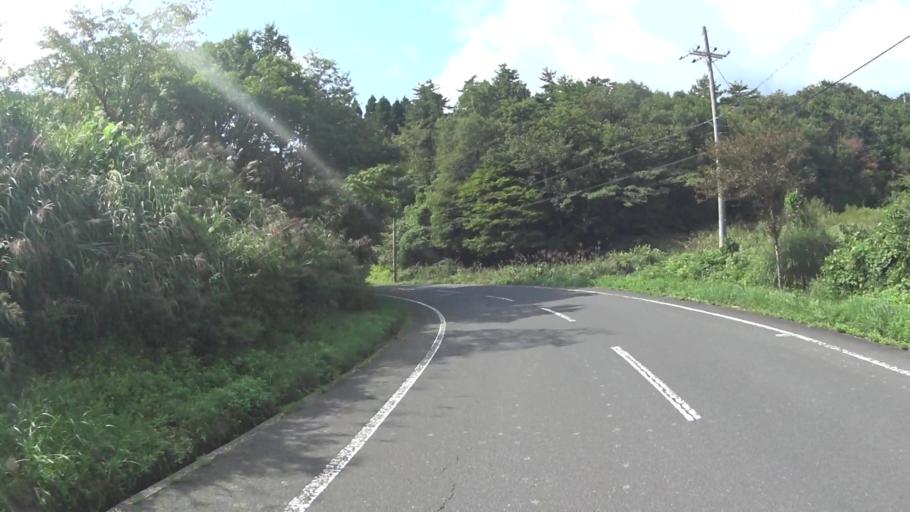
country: JP
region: Kyoto
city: Miyazu
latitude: 35.6438
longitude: 135.1845
